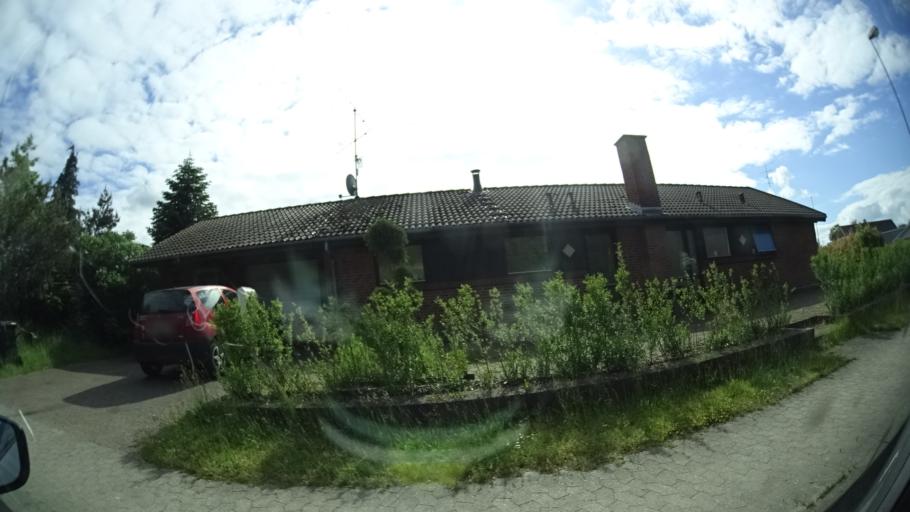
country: DK
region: Central Jutland
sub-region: Norddjurs Kommune
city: Grenaa
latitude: 56.5269
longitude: 10.7115
